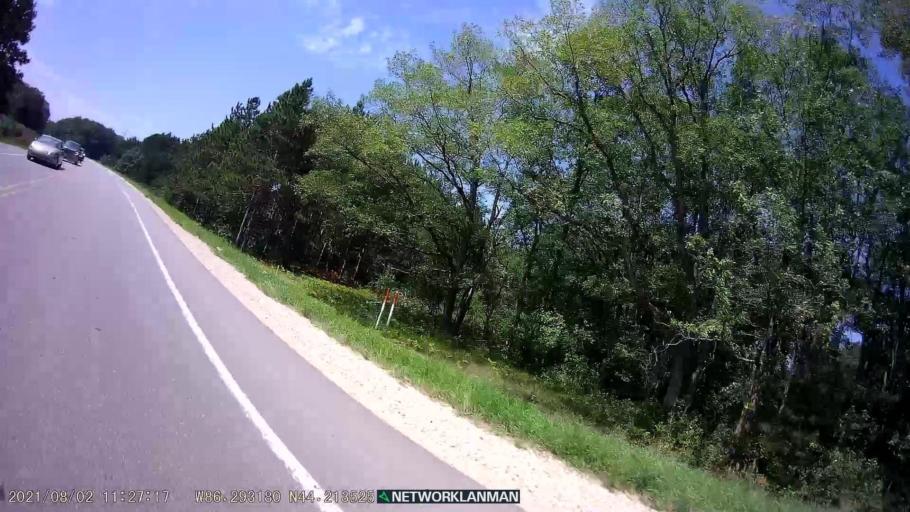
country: US
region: Michigan
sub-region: Manistee County
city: Manistee
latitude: 44.2136
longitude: -86.2937
